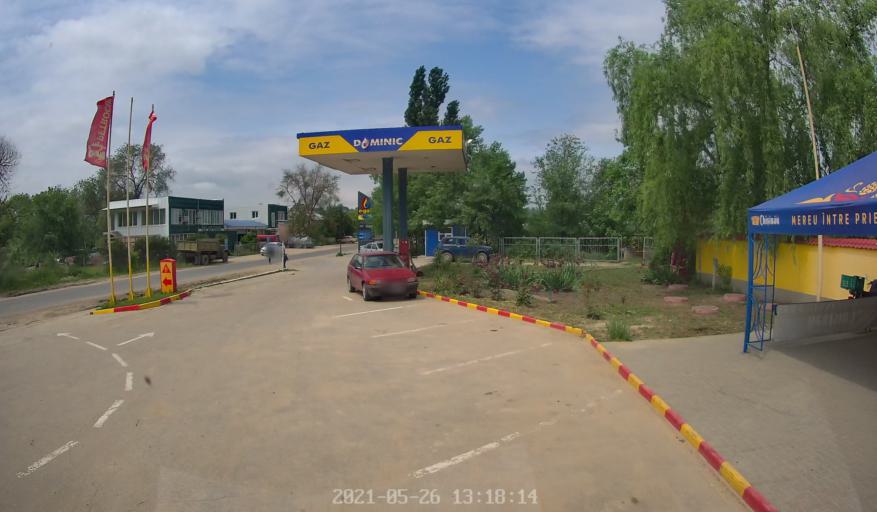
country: MD
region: Hincesti
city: Dancu
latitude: 46.7614
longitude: 28.3509
